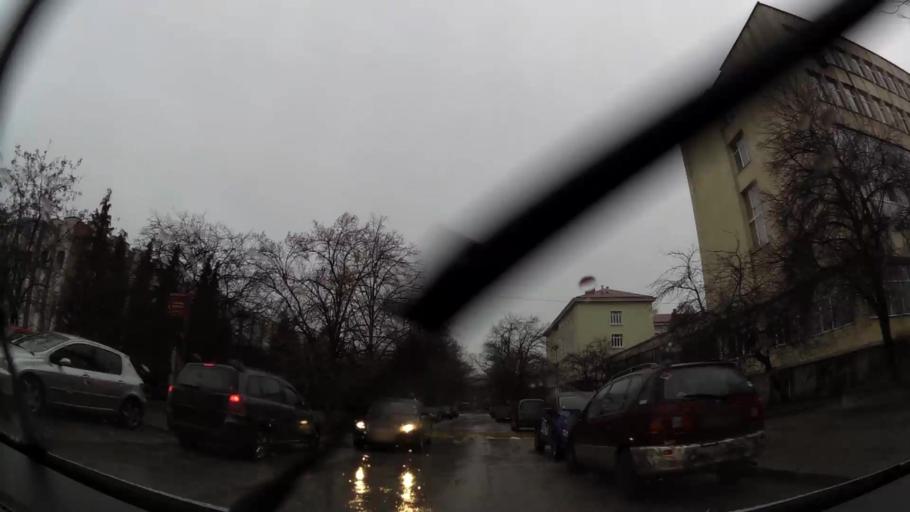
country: BG
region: Sofia-Capital
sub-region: Stolichna Obshtina
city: Sofia
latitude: 42.6582
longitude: 23.3544
